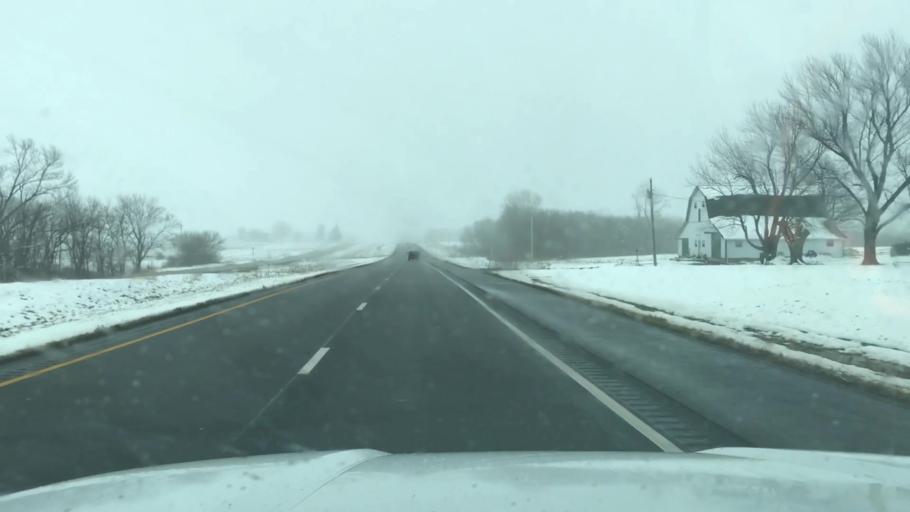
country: US
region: Missouri
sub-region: DeKalb County
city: Maysville
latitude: 39.7614
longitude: -94.3970
